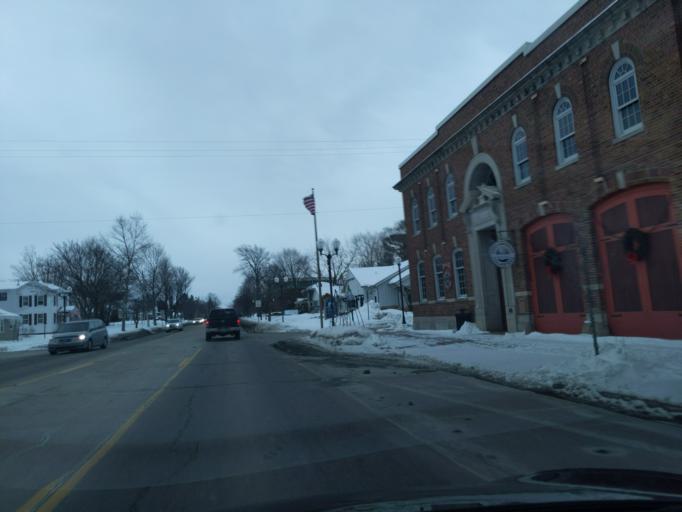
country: US
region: Michigan
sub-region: Ottawa County
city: Spring Lake
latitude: 43.0767
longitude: -86.1977
